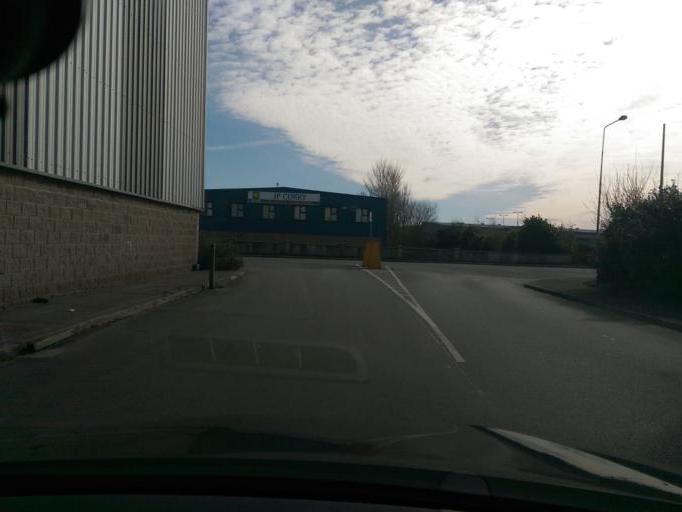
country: IE
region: Connaught
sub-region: County Galway
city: Oranmore
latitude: 53.2818
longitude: -8.9312
